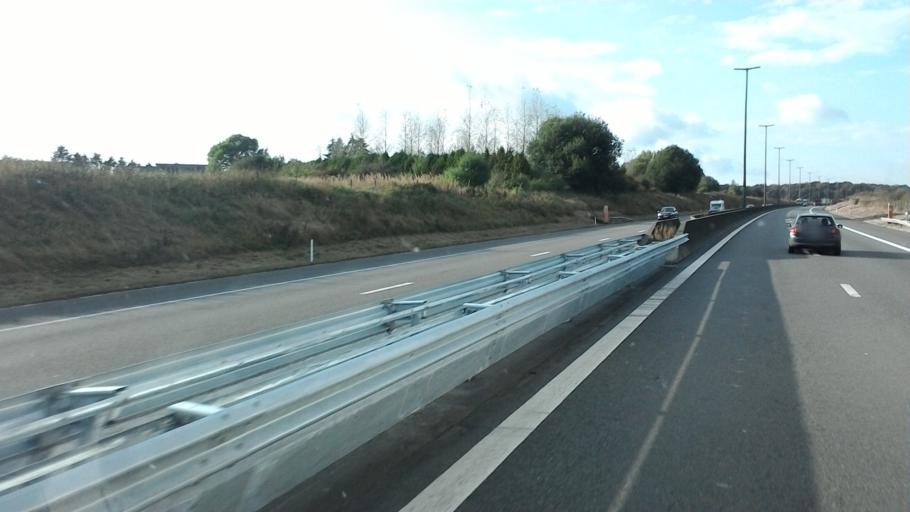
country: BE
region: Wallonia
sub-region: Province du Luxembourg
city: Habay-la-Vieille
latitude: 49.7240
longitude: 5.5867
